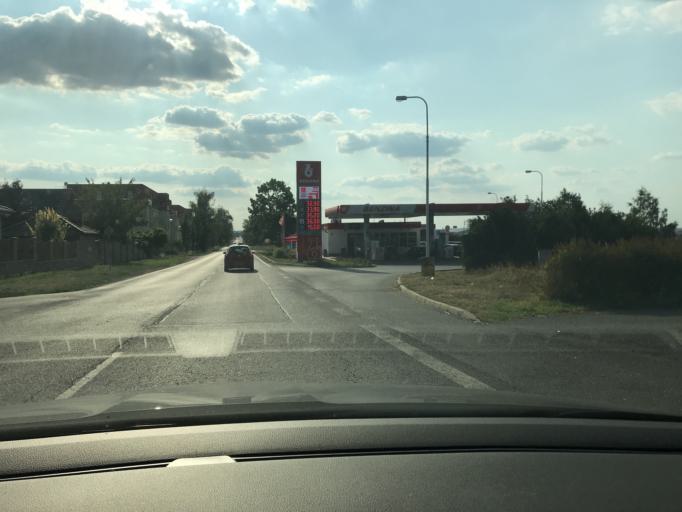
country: CZ
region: Central Bohemia
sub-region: Okres Kladno
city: Slany
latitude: 50.2352
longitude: 14.0712
